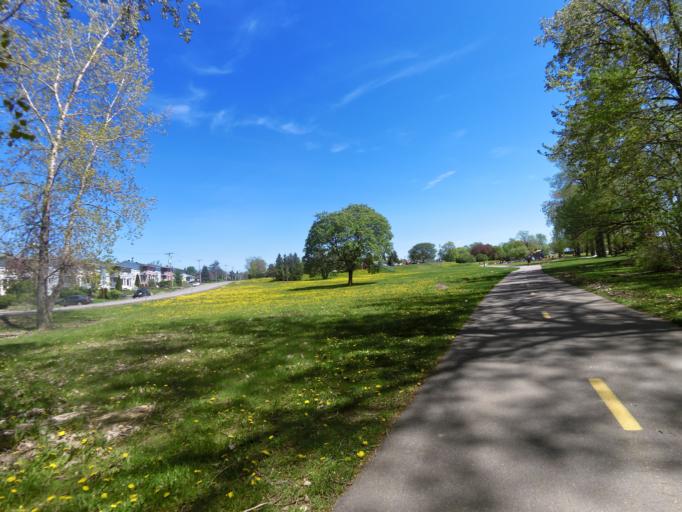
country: CA
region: Ontario
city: Bells Corners
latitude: 45.4001
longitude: -75.8633
